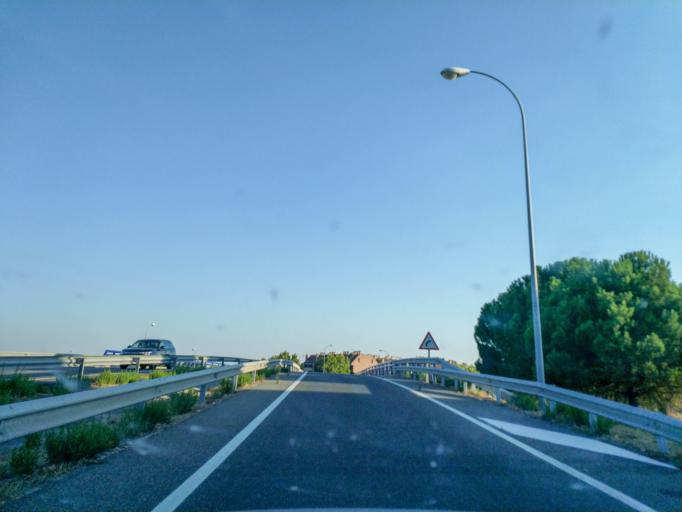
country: ES
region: Madrid
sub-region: Provincia de Madrid
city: Pozuelo de Alarcon
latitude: 40.4614
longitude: -3.8092
